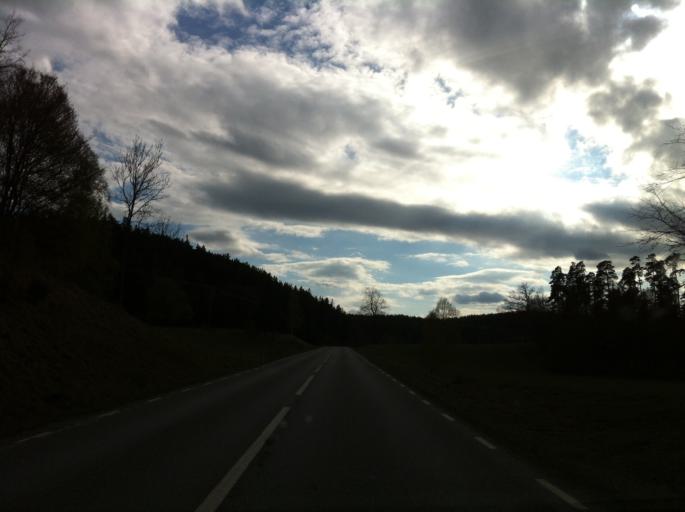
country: SE
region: OEstergoetland
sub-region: Kinda Kommun
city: Rimforsa
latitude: 58.0715
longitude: 15.8286
